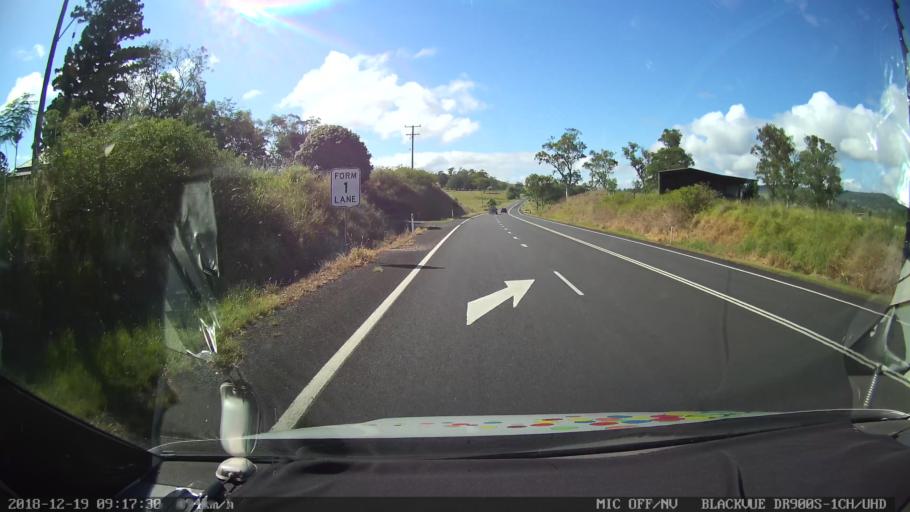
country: AU
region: New South Wales
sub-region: Kyogle
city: Kyogle
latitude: -28.5346
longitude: 152.9744
